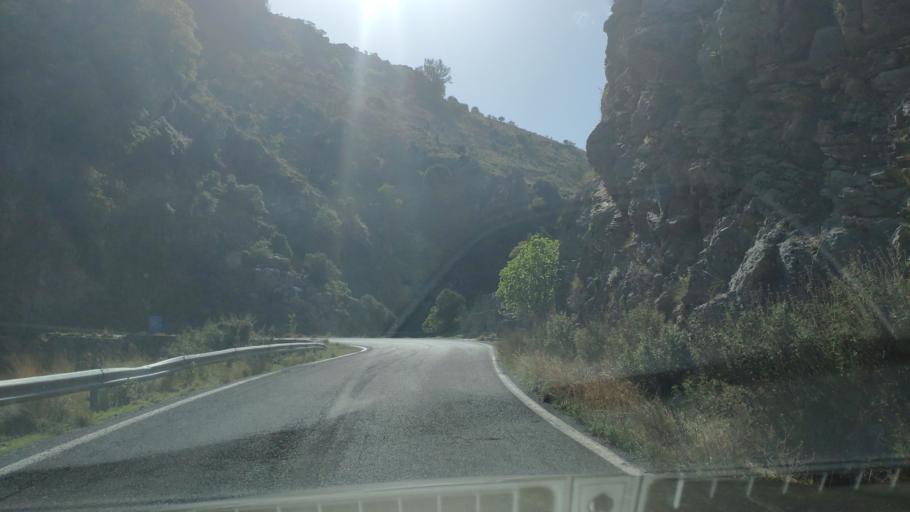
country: GR
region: Peloponnese
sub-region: Nomos Arkadias
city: Dimitsana
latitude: 37.5984
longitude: 22.0282
